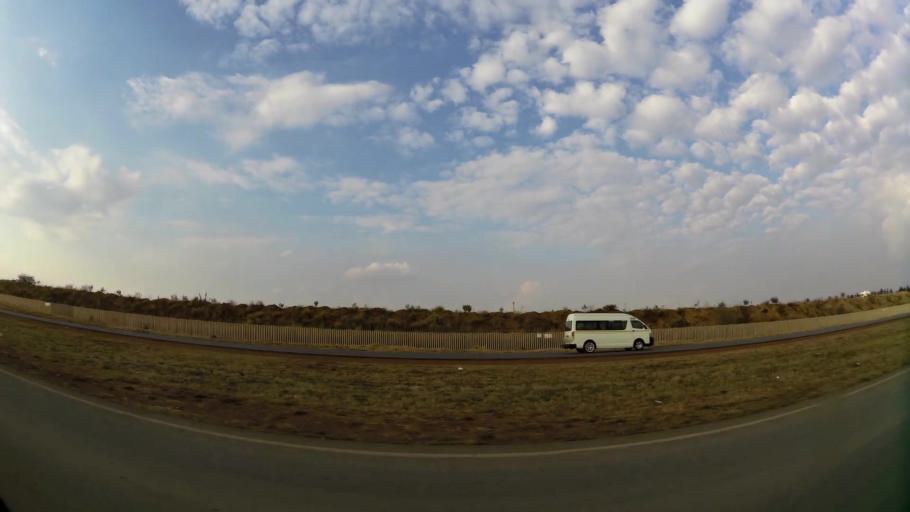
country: ZA
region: Gauteng
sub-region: Sedibeng District Municipality
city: Vereeniging
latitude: -26.6418
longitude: 27.8734
